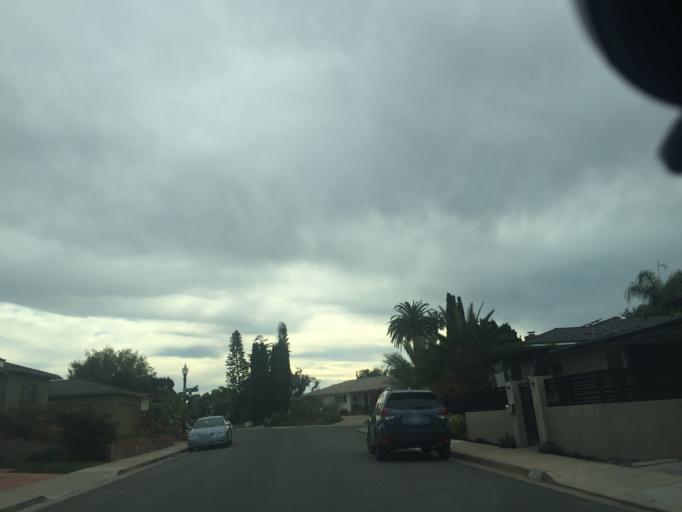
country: US
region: California
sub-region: San Diego County
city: Lemon Grove
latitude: 32.7686
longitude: -117.0935
